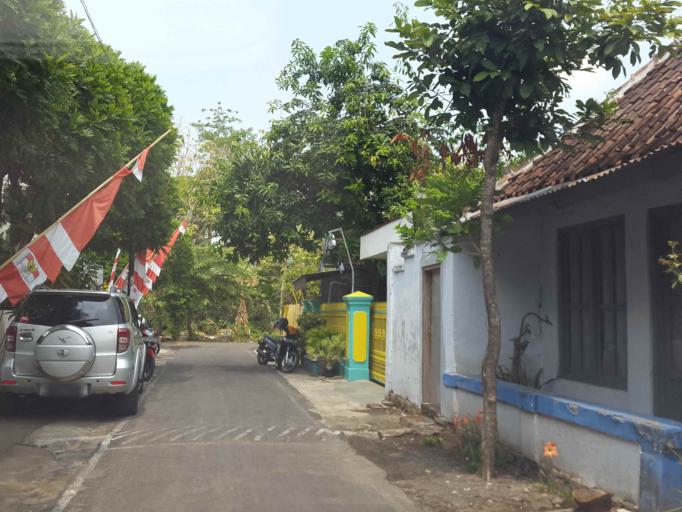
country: ID
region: Central Java
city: Jaten
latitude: -7.5970
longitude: 110.9535
